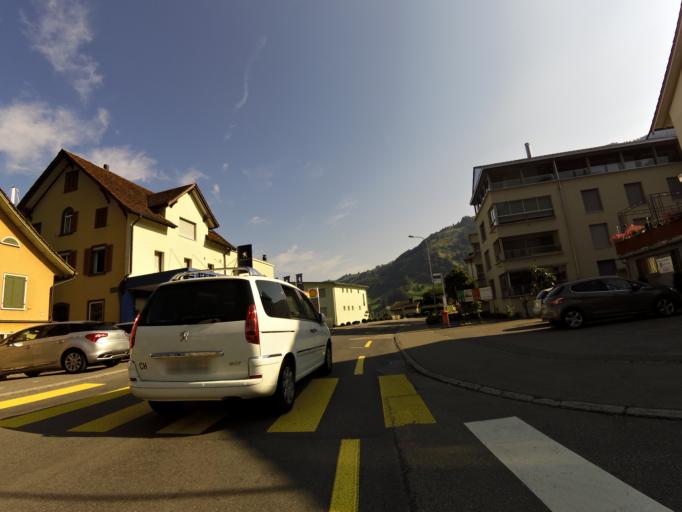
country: CH
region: Schwyz
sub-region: Bezirk Schwyz
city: Arth
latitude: 47.0645
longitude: 8.5229
